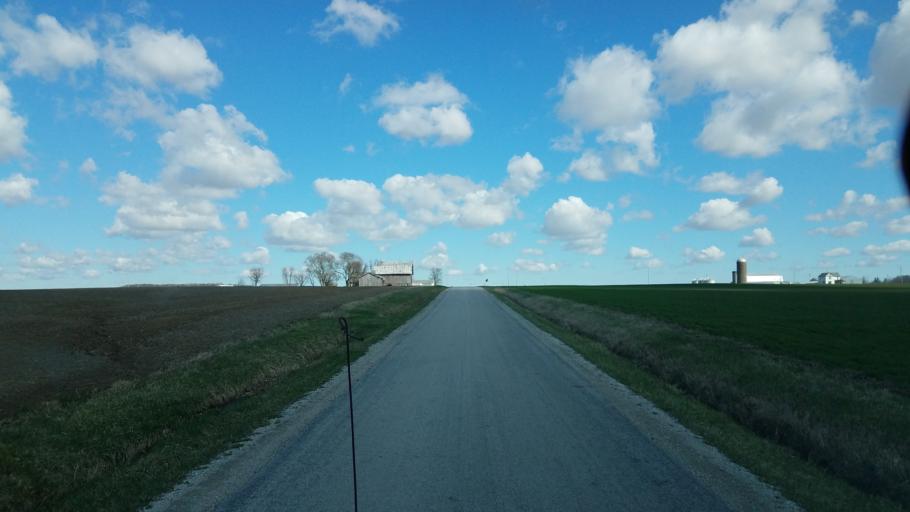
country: US
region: Ohio
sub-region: Sandusky County
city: Mount Carmel
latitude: 41.0772
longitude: -82.9389
